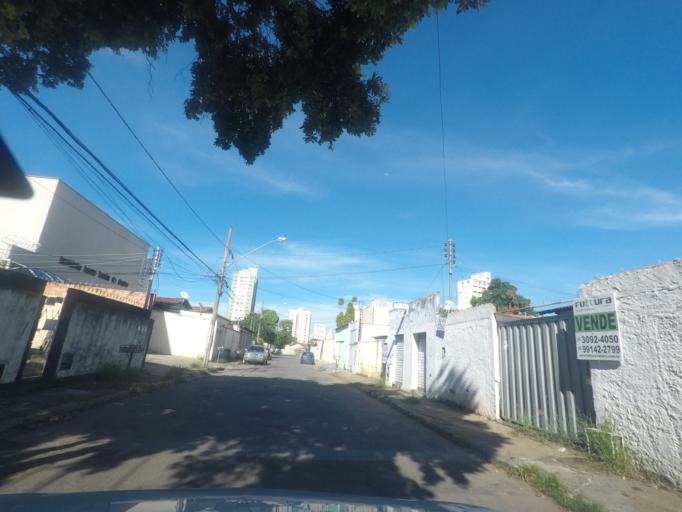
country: BR
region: Goias
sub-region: Goiania
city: Goiania
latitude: -16.6687
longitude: -49.2634
